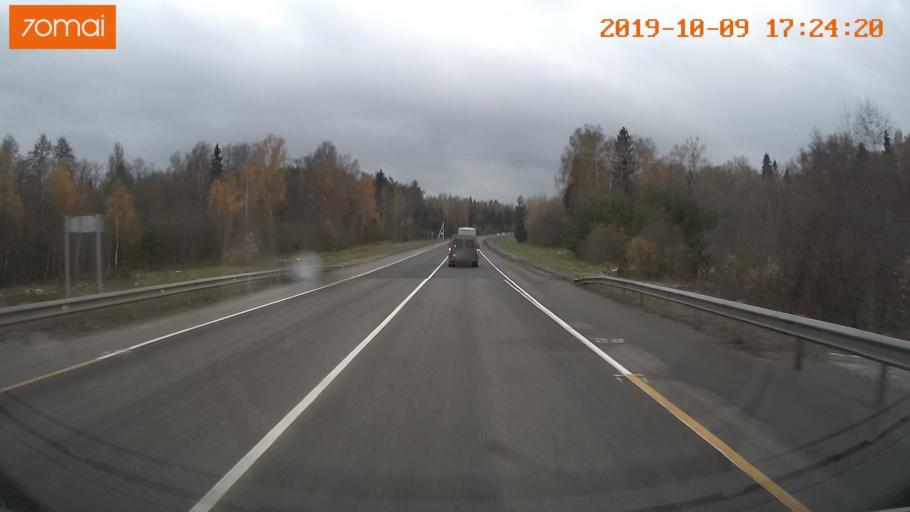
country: RU
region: Ivanovo
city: Furmanov
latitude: 57.1862
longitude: 41.1085
